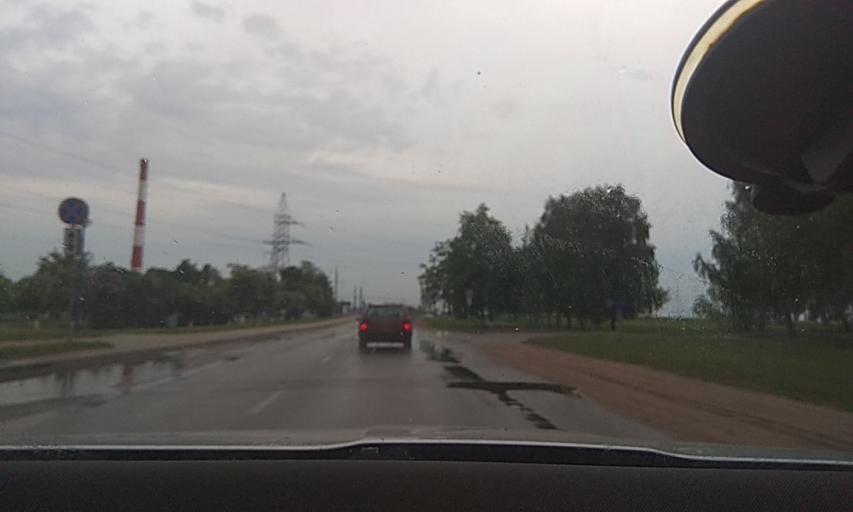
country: BY
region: Grodnenskaya
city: Hrodna
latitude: 53.6746
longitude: 23.8896
